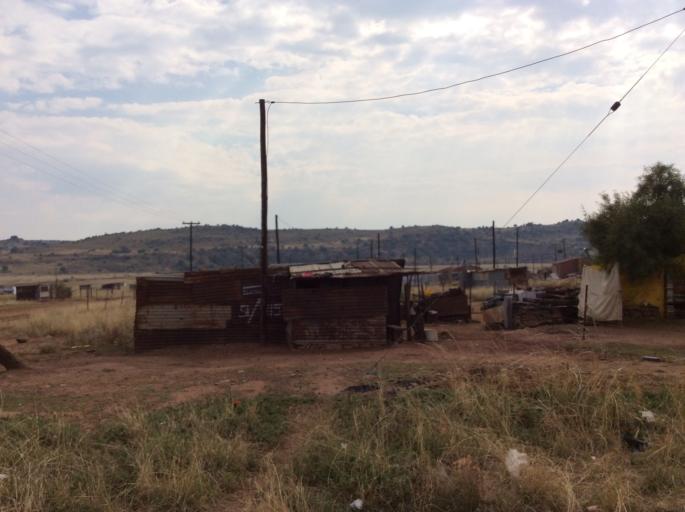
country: LS
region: Mafeteng
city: Mafeteng
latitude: -29.9878
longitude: 27.0016
